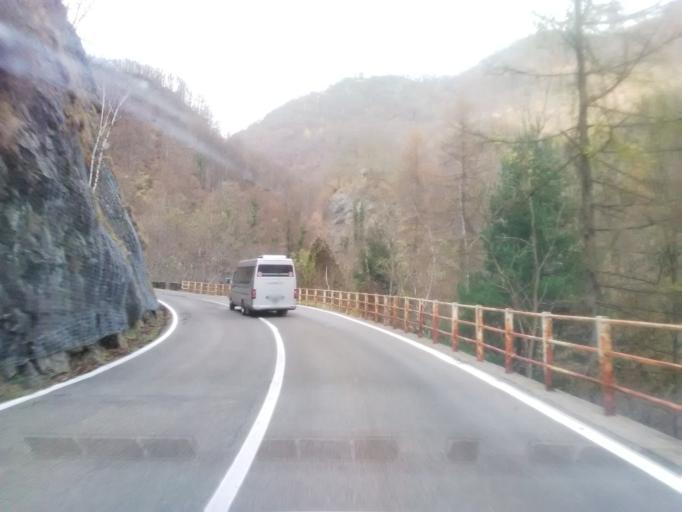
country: IT
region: Piedmont
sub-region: Provincia di Vercelli
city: Sabbia
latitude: 45.8430
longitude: 8.2500
